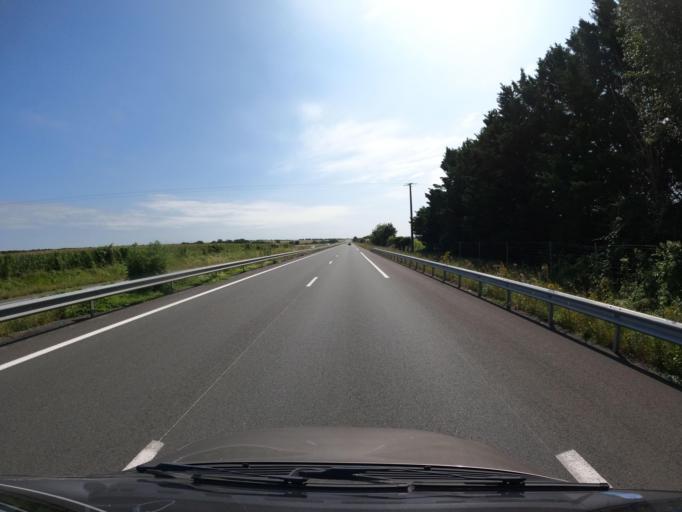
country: FR
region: Poitou-Charentes
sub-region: Departement des Deux-Sevres
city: Mauze-sur-le-Mignon
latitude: 46.2044
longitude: -0.7231
